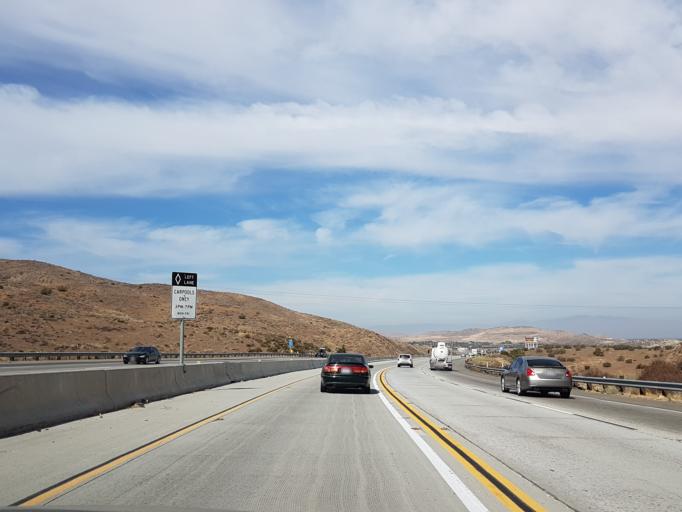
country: US
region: California
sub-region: Los Angeles County
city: Vincent
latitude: 34.5349
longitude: -118.1173
